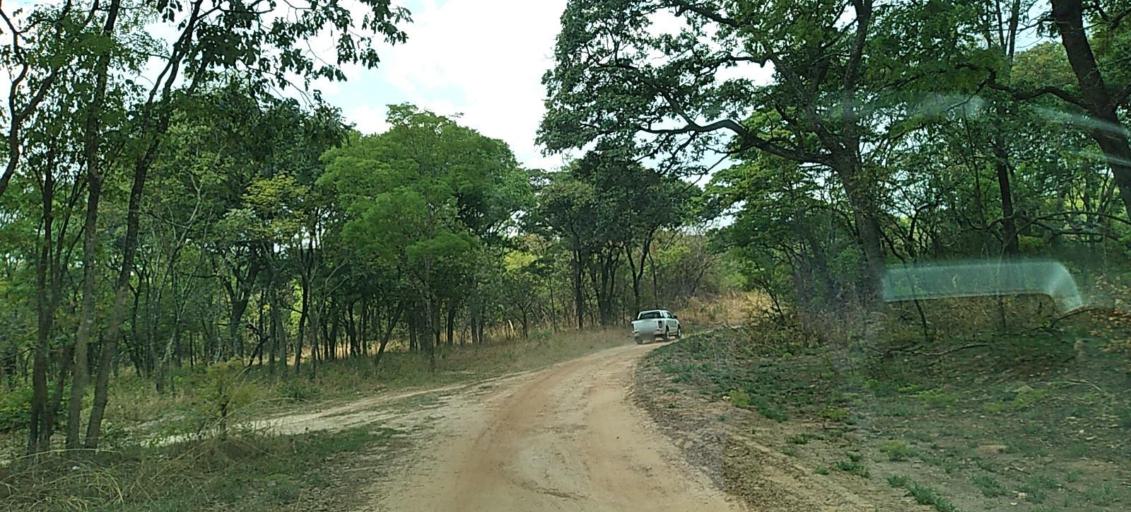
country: ZM
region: Copperbelt
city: Chingola
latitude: -12.7911
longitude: 27.6449
